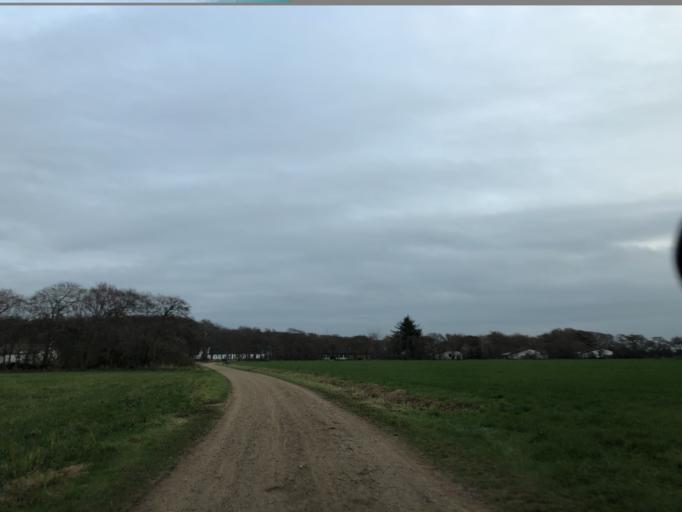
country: DK
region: Central Jutland
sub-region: Holstebro Kommune
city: Ulfborg
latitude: 56.2776
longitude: 8.2301
